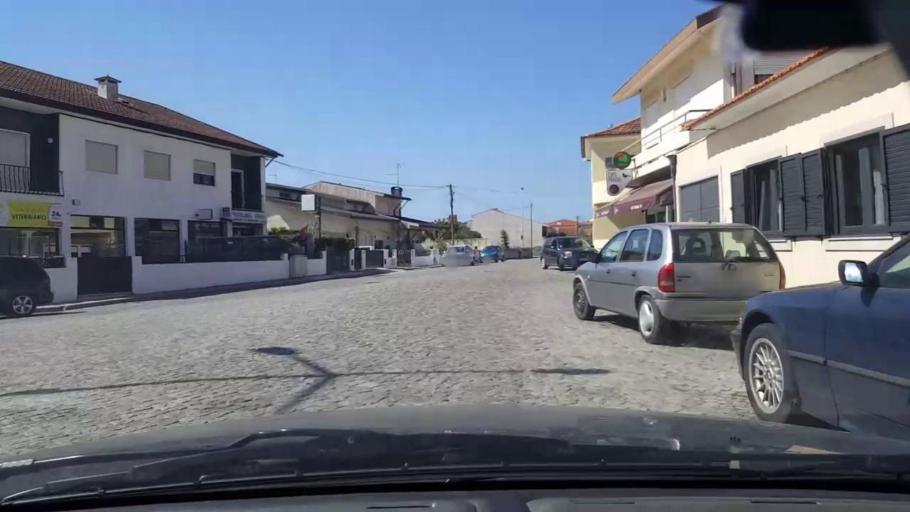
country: PT
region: Porto
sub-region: Matosinhos
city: Lavra
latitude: 41.2787
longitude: -8.7196
